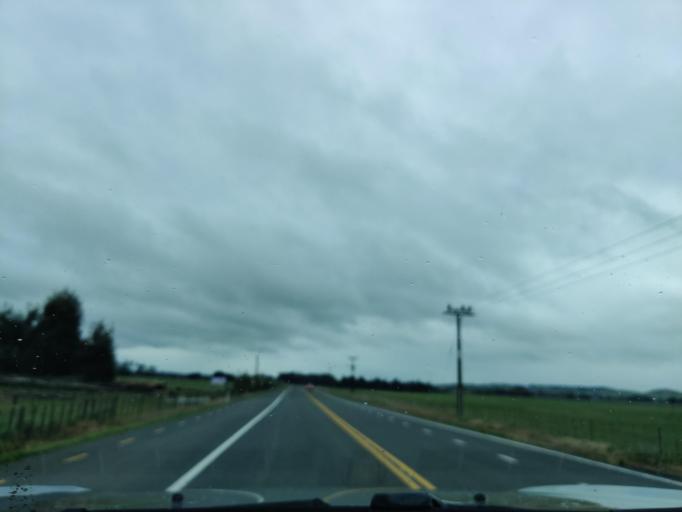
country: NZ
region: Hawke's Bay
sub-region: Hastings District
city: Hastings
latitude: -40.0018
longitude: 176.3972
